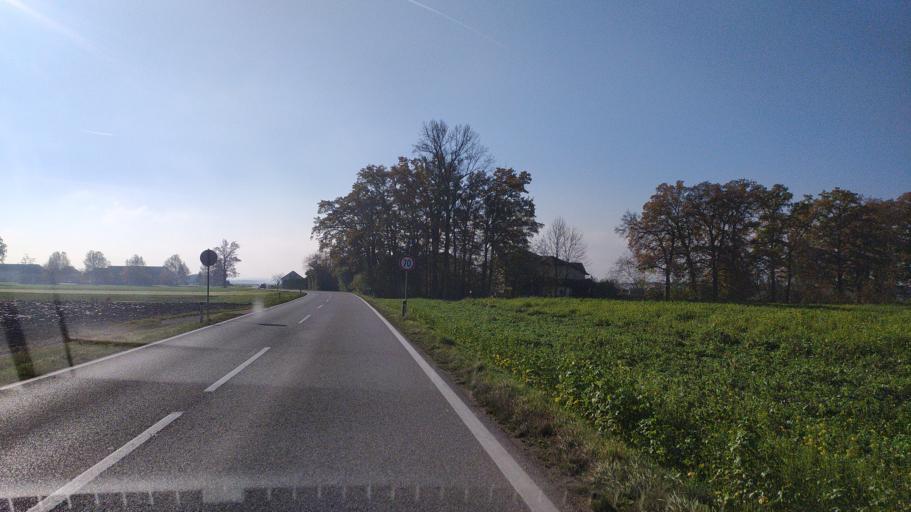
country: AT
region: Upper Austria
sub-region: Politischer Bezirk Perg
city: Perg
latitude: 48.2347
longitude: 14.6227
